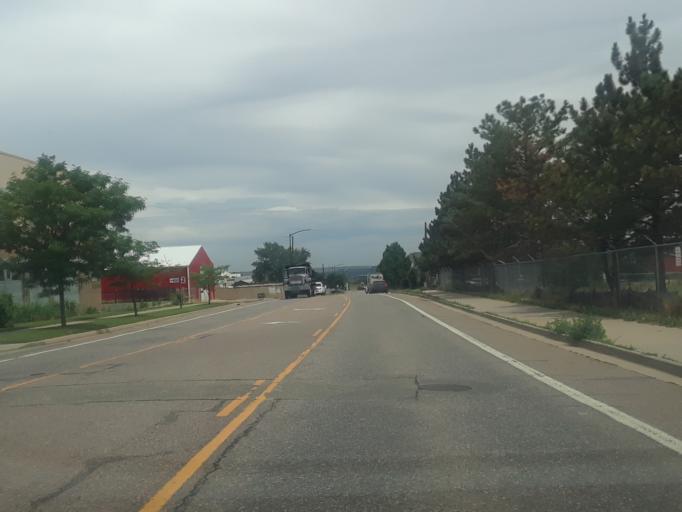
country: US
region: Colorado
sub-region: Boulder County
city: Boulder
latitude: 40.0618
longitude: -105.2813
